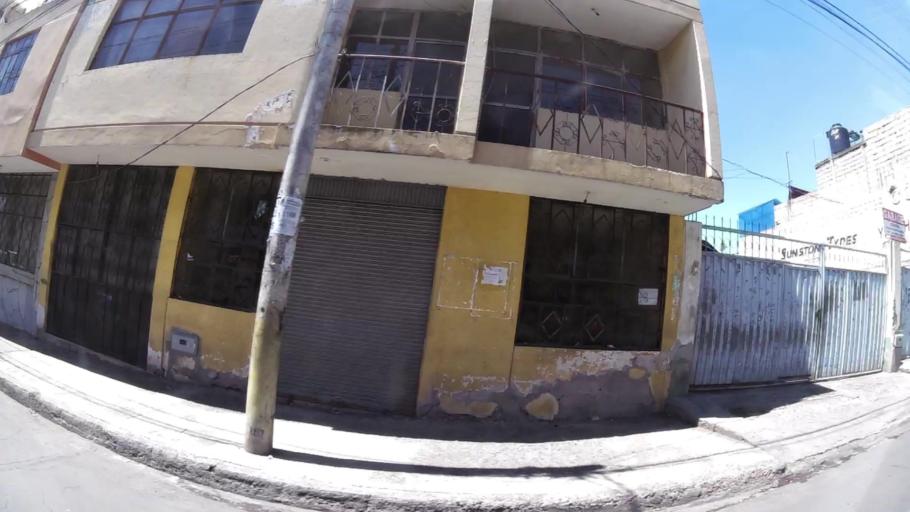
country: EC
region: Chimborazo
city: Riobamba
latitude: -1.6695
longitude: -78.6571
